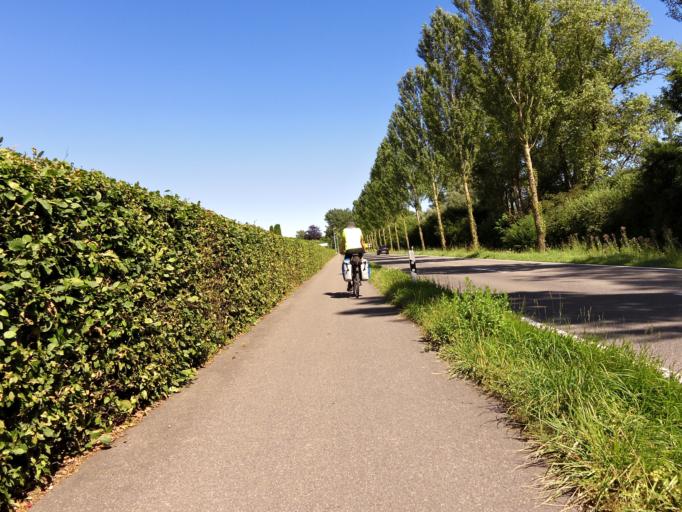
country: DE
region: Baden-Wuerttemberg
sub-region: Freiburg Region
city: Moos
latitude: 47.7393
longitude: 8.9444
